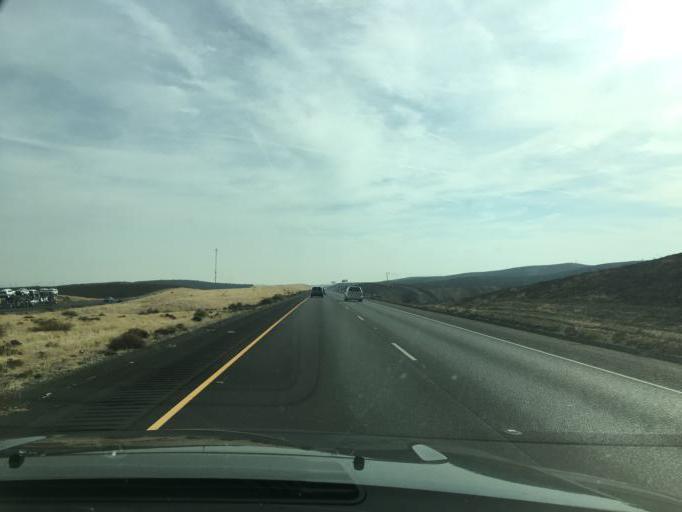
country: US
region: California
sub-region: Kings County
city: Kettleman City
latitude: 36.0196
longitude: -120.0060
